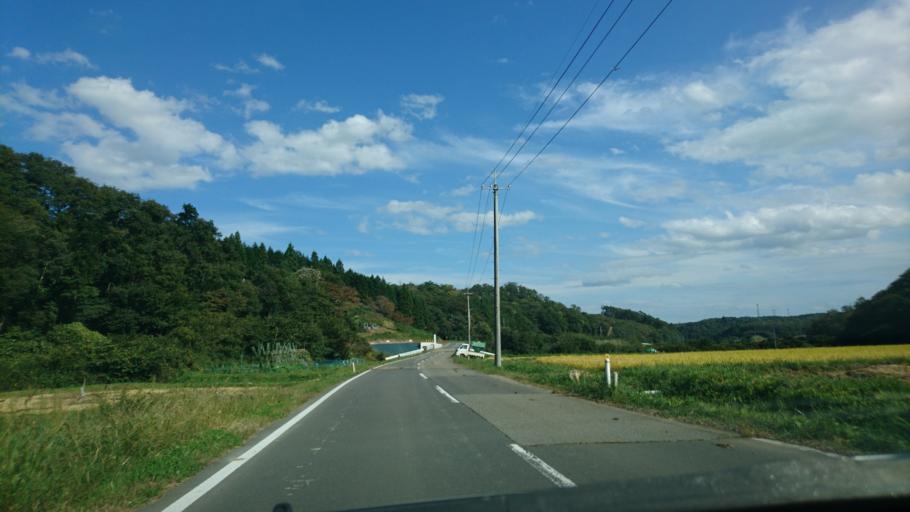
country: JP
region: Iwate
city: Ichinoseki
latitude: 38.8740
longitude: 141.0835
